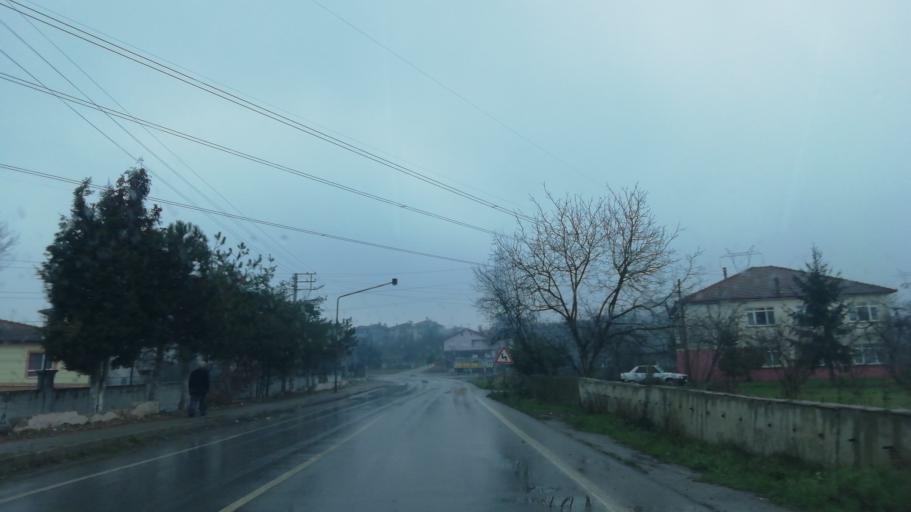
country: TR
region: Sakarya
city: Karapurcek
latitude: 40.6884
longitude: 30.5079
